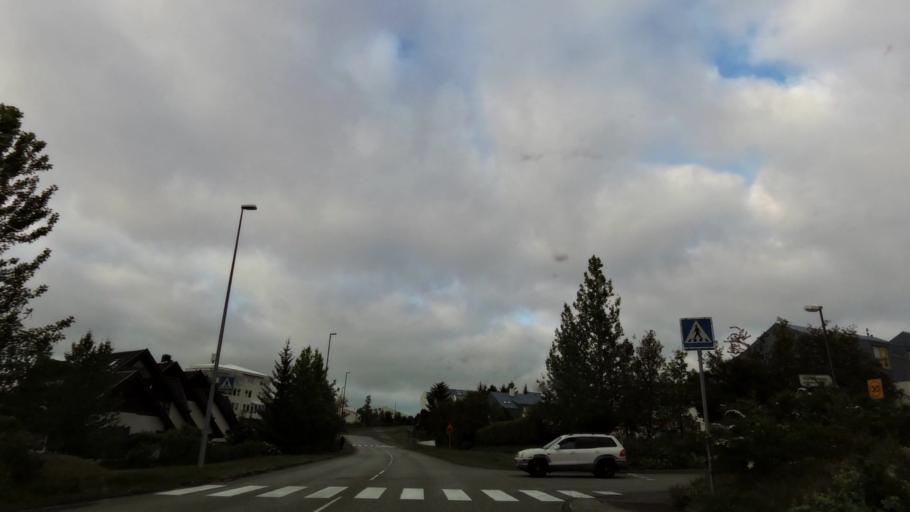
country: IS
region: Capital Region
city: Hafnarfjoerdur
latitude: 64.0593
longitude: -21.9551
